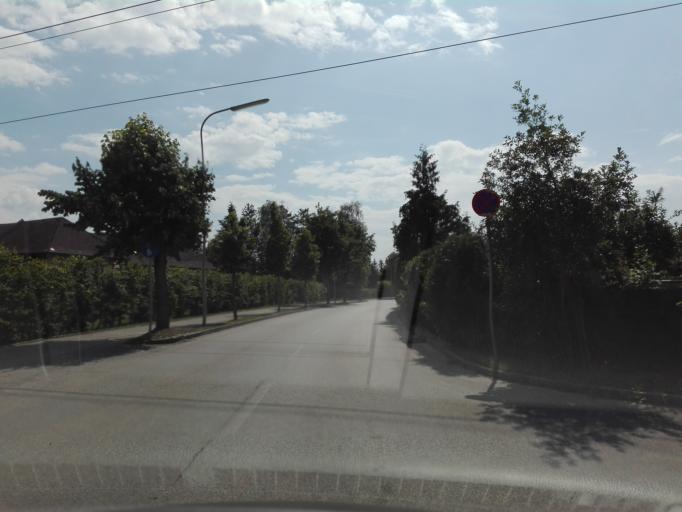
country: AT
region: Upper Austria
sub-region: Politischer Bezirk Linz-Land
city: Traun
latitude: 48.2121
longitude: 14.2160
